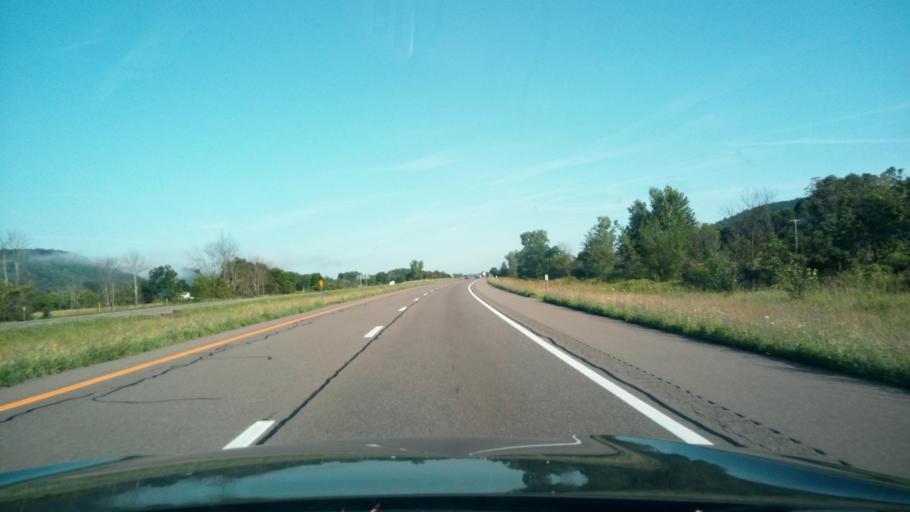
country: US
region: New York
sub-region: Steuben County
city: Bath
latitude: 42.2955
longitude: -77.2352
